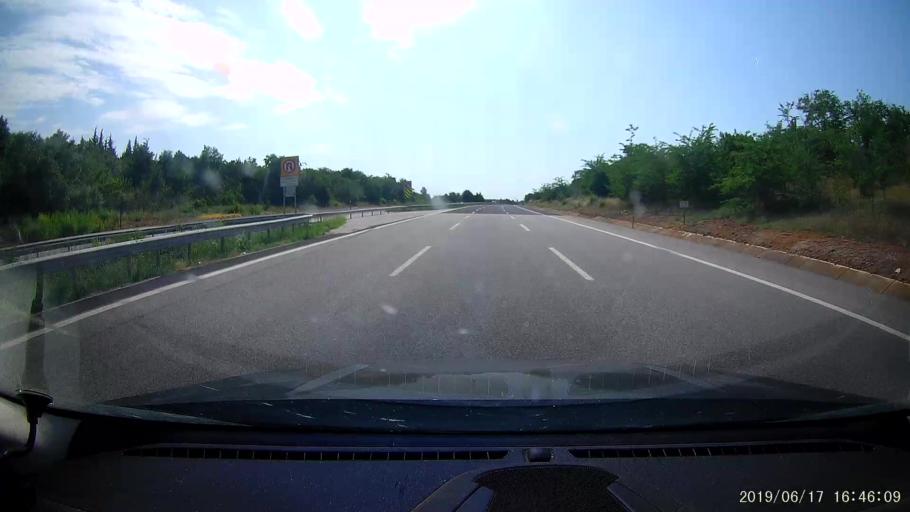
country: TR
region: Kirklareli
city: Babaeski
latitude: 41.4944
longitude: 27.2120
